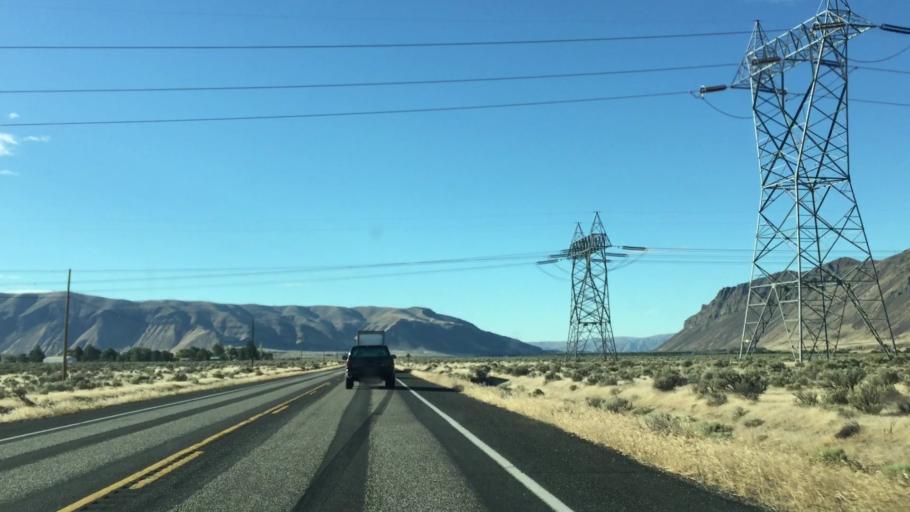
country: US
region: Washington
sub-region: Grant County
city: Mattawa
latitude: 46.8681
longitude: -119.9560
